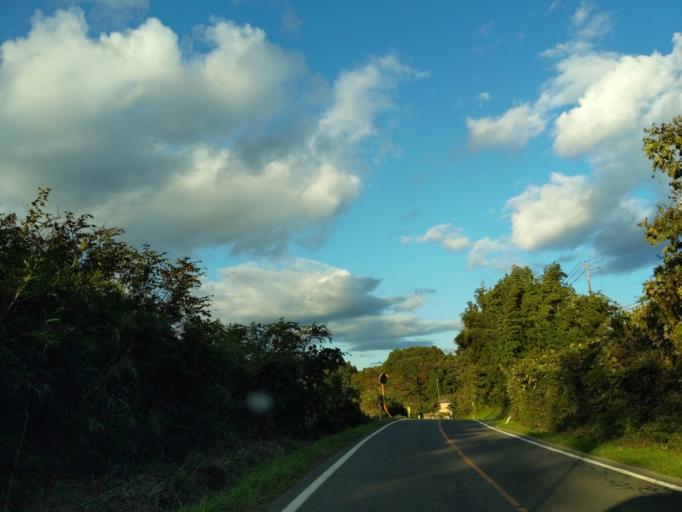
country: JP
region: Fukushima
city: Miharu
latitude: 37.4441
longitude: 140.4254
